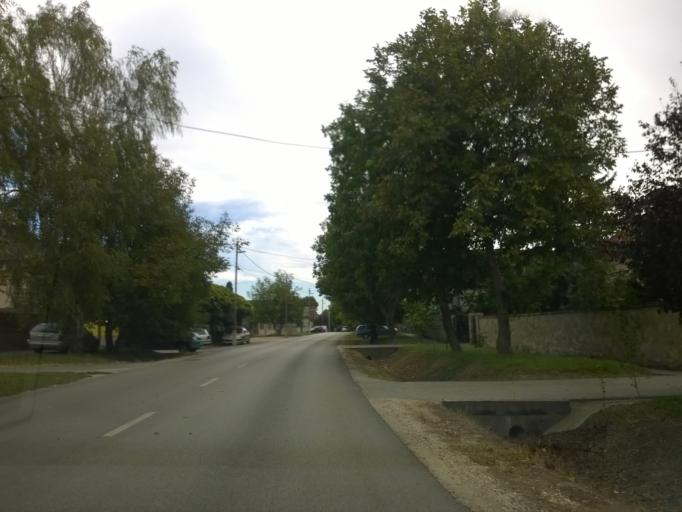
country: HU
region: Pest
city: Szigetszentmiklos
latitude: 47.3523
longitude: 19.0396
